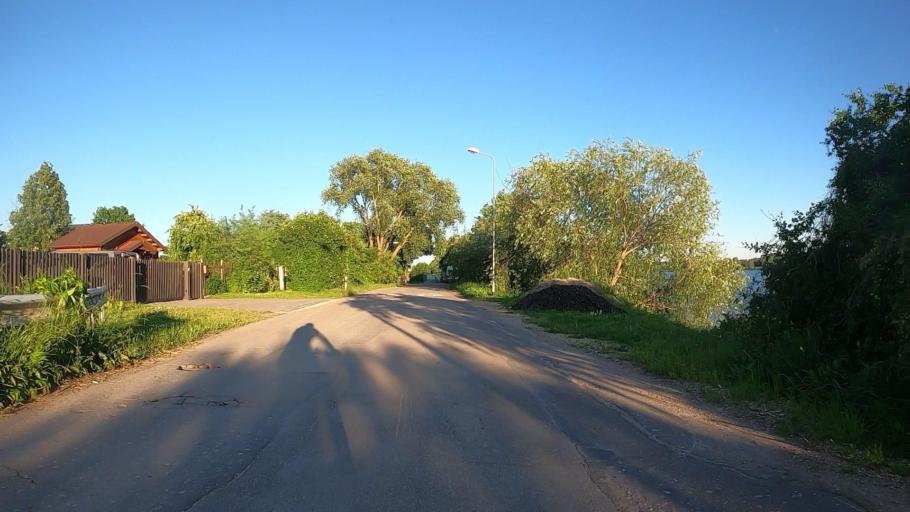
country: LV
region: Kekava
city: Kekava
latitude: 56.8667
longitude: 24.2549
